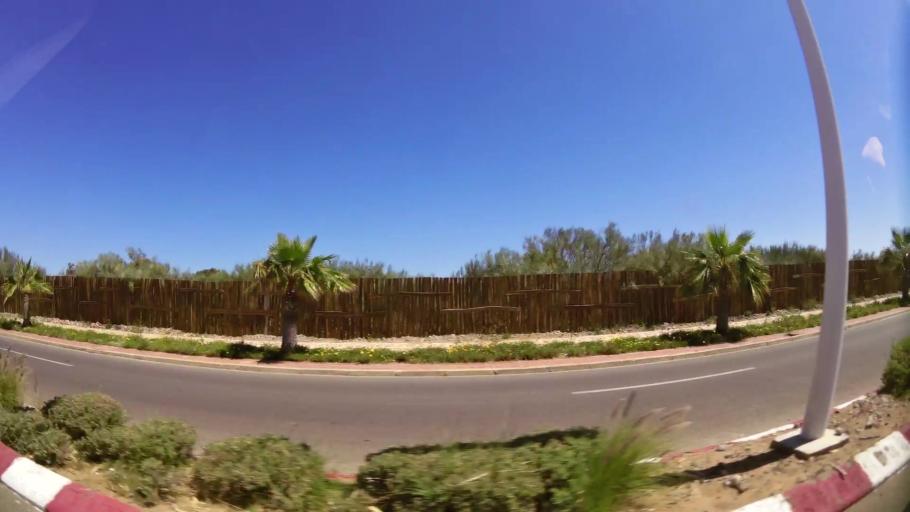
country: MA
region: Oriental
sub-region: Berkane-Taourirt
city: Madagh
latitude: 35.0958
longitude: -2.2725
